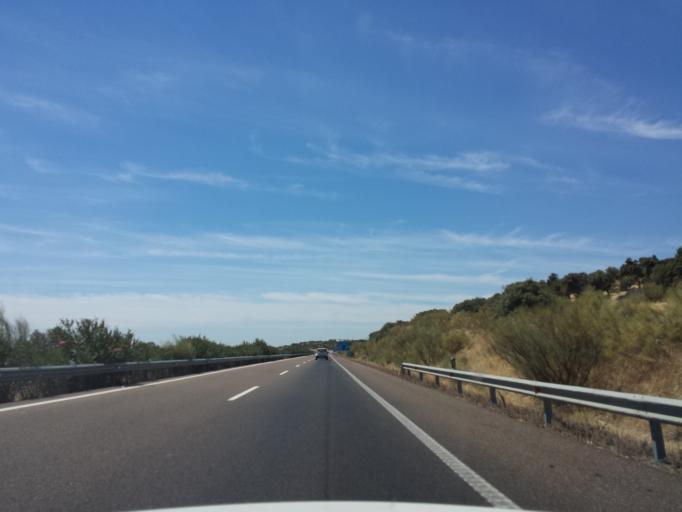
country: ES
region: Extremadura
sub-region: Provincia de Badajoz
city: San Pedro de Merida
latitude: 38.9566
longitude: -6.1614
